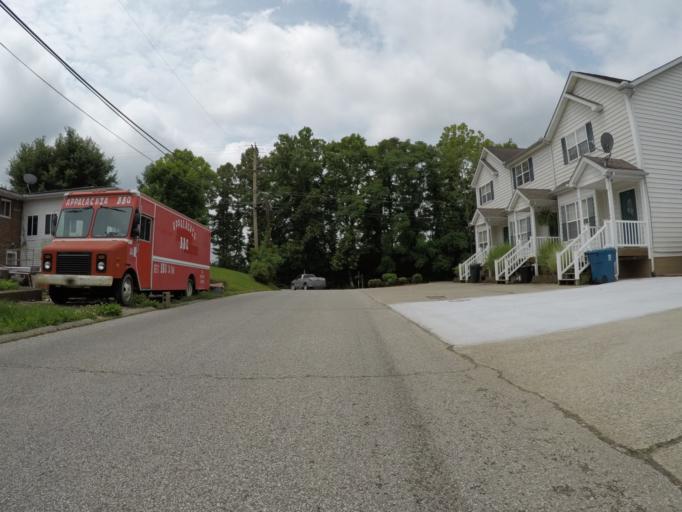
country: US
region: West Virginia
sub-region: Cabell County
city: Pea Ridge
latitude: 38.4150
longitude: -82.3401
